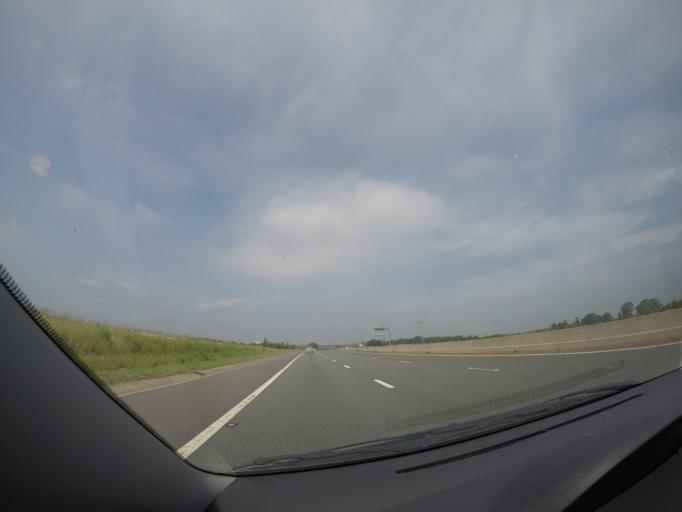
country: GB
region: England
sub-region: North Yorkshire
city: Bedale
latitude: 54.2690
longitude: -1.5234
